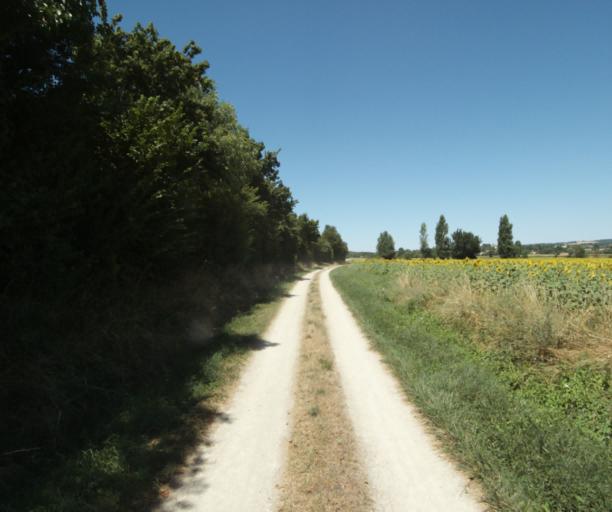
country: FR
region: Midi-Pyrenees
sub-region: Departement de la Haute-Garonne
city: Saint-Felix-Lauragais
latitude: 43.4655
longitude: 1.9271
